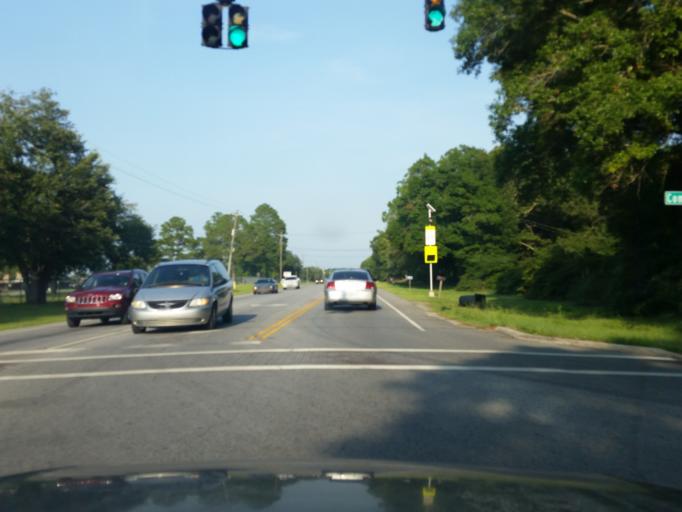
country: US
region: Florida
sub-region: Escambia County
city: Bellview
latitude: 30.4865
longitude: -87.2980
